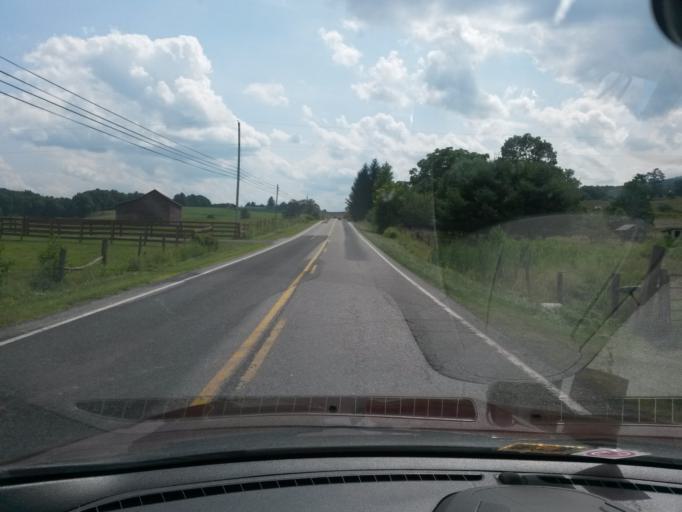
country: US
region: Virginia
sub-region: Highland County
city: Monterey
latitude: 38.4234
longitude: -79.5685
